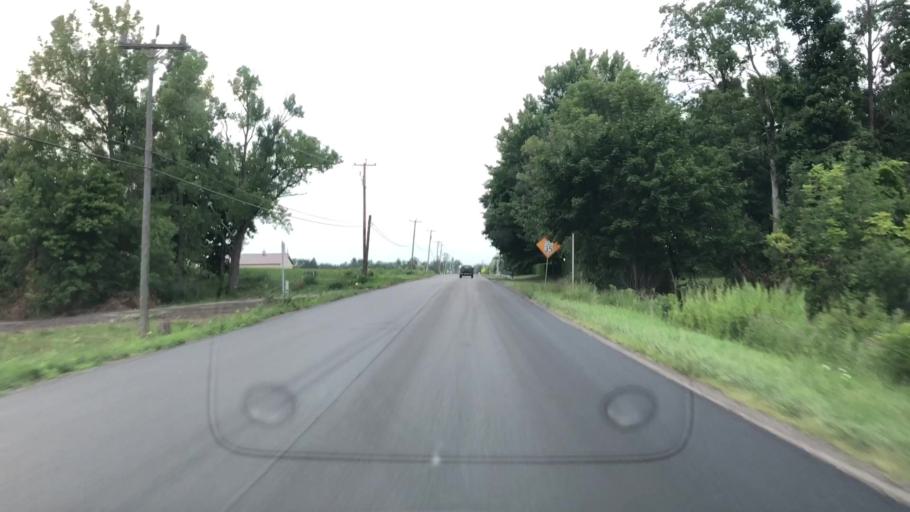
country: US
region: New York
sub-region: Erie County
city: Elma Center
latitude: 42.8300
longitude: -78.6060
